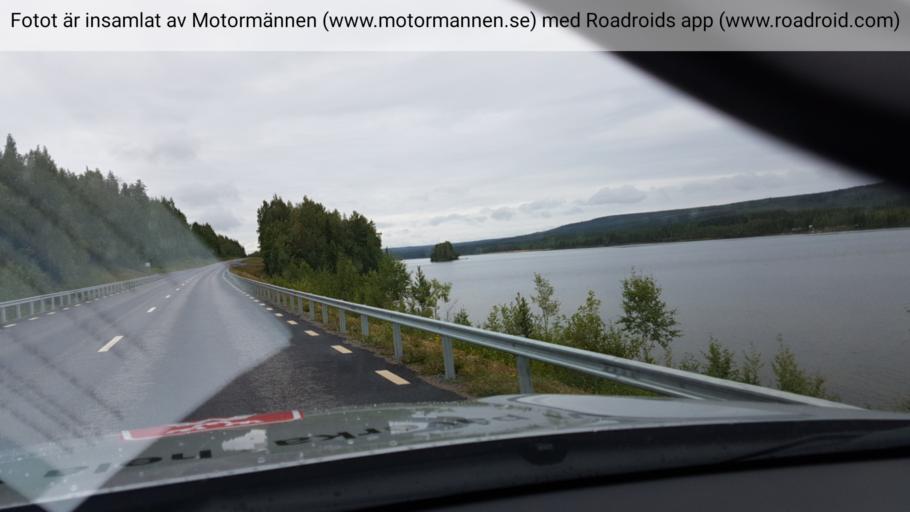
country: SE
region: Norrbotten
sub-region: Alvsbyns Kommun
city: AElvsbyn
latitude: 66.2635
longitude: 20.8353
